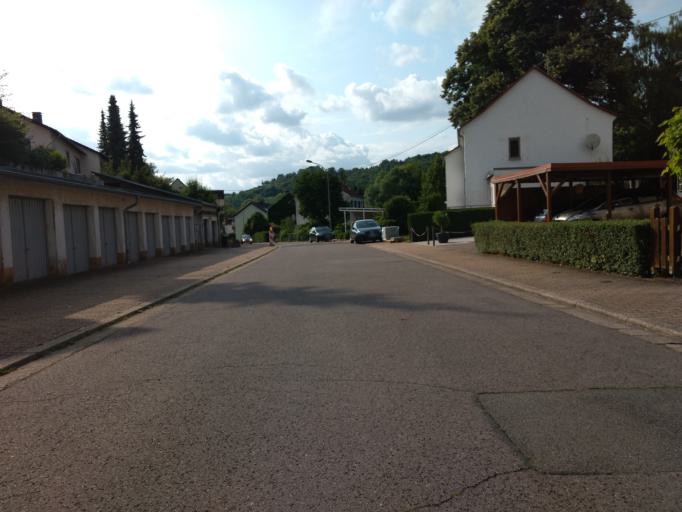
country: DE
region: Saarland
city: Merzig
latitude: 49.4420
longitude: 6.6516
